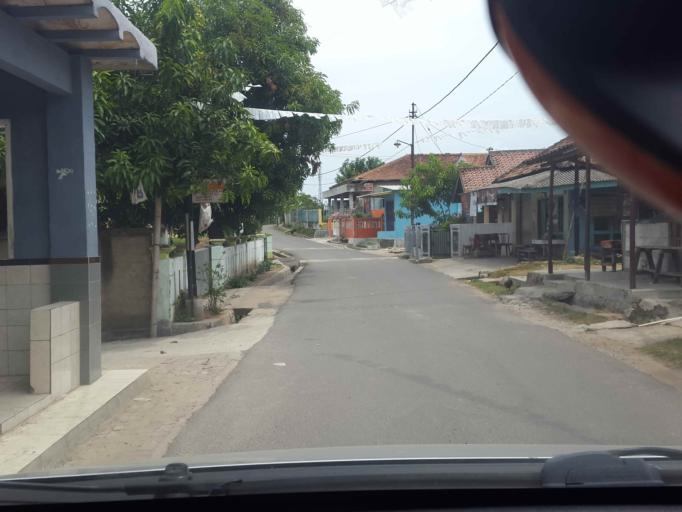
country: ID
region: Lampung
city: Panjang
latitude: -5.4375
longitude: 105.3009
